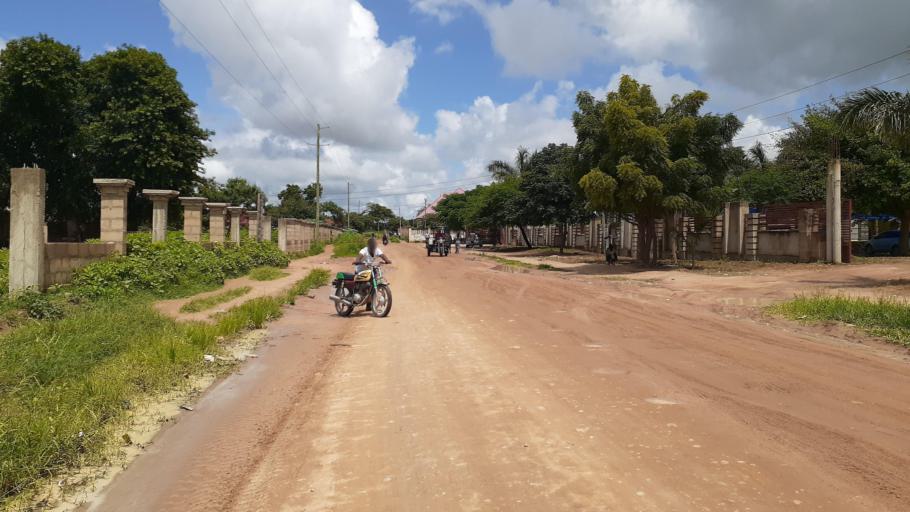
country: TZ
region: Dodoma
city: Dodoma
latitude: -6.1230
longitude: 35.7408
